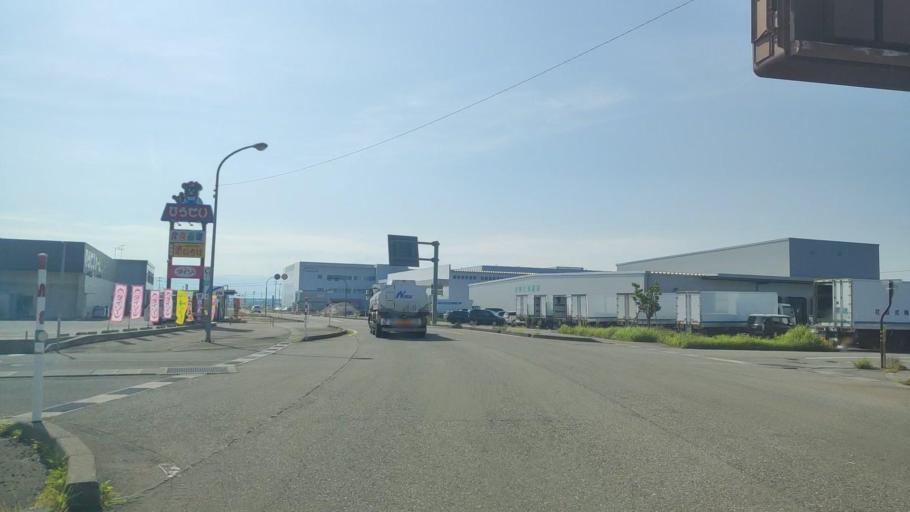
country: JP
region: Ishikawa
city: Matsuto
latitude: 36.5018
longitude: 136.5017
